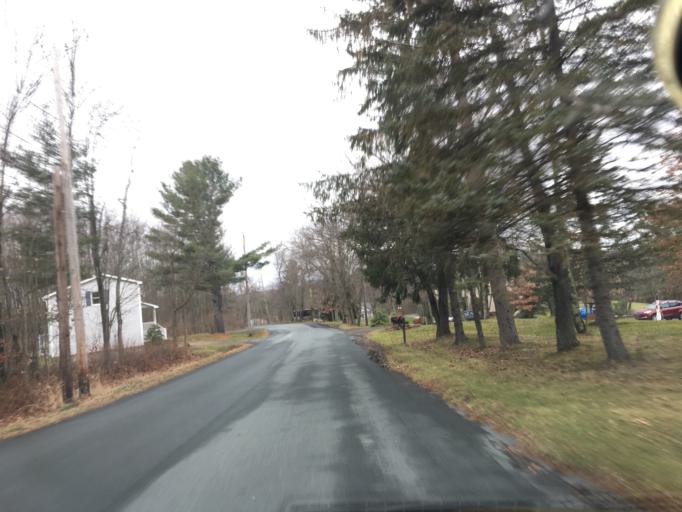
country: US
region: New York
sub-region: Rensselaer County
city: Averill Park
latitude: 42.6133
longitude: -73.5592
